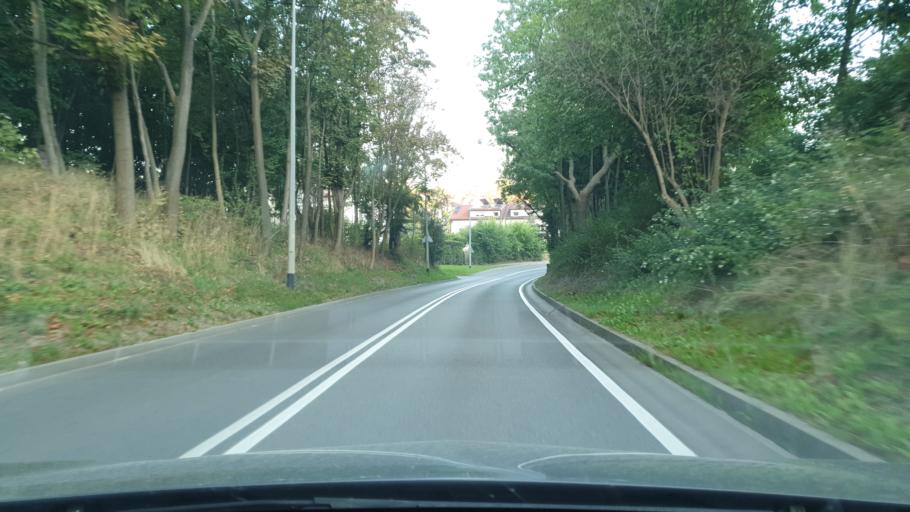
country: PL
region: Pomeranian Voivodeship
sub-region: Gdansk
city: Gdansk
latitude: 54.3573
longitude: 18.5917
